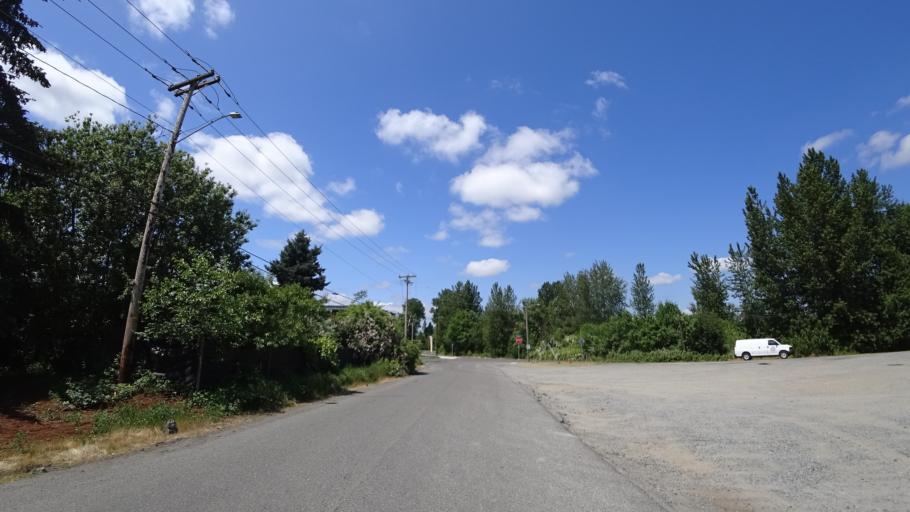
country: US
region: Washington
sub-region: Clark County
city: Vancouver
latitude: 45.5991
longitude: -122.6587
